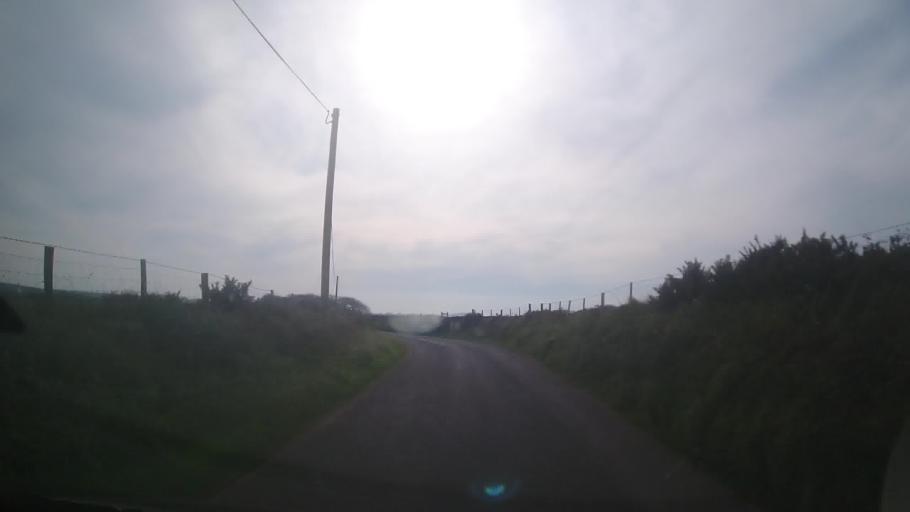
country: GB
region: Wales
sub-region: Pembrokeshire
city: Saint David's
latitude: 51.9159
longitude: -5.2374
